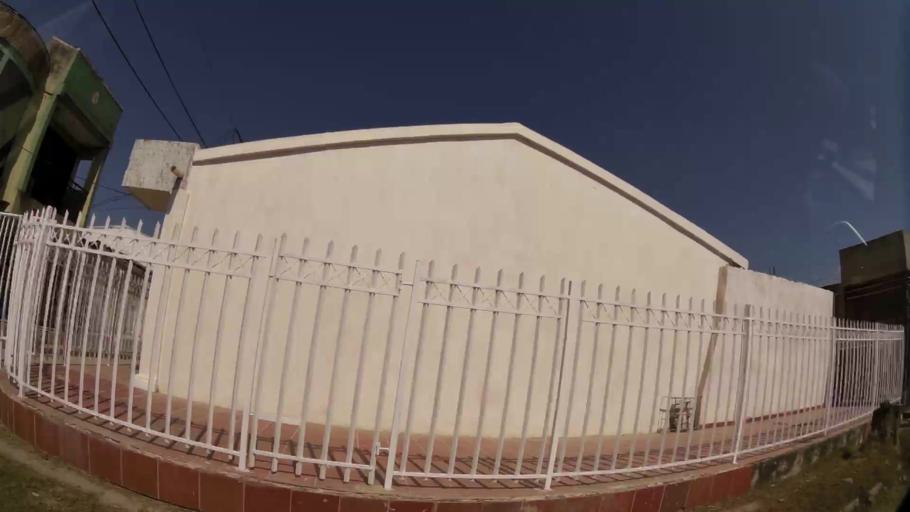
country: CO
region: Bolivar
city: Cartagena
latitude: 10.3773
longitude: -75.4662
